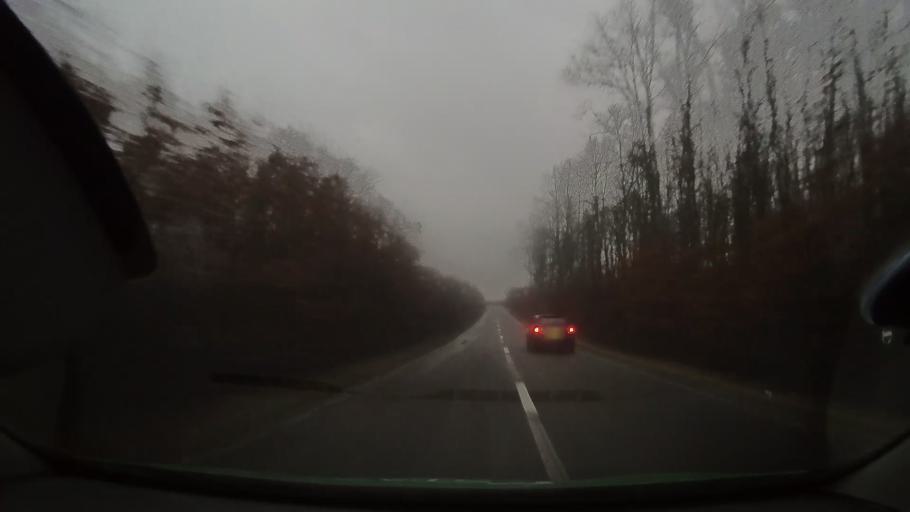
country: RO
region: Arad
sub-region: Comuna Beliu
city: Beliu
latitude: 46.5221
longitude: 21.9545
